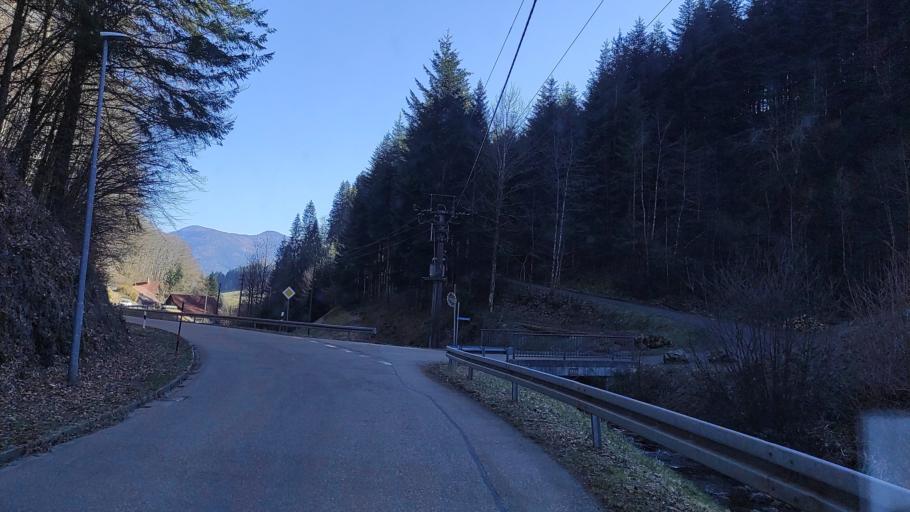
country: DE
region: Baden-Wuerttemberg
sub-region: Freiburg Region
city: Gutach im Breisgau
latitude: 48.1671
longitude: 8.0073
